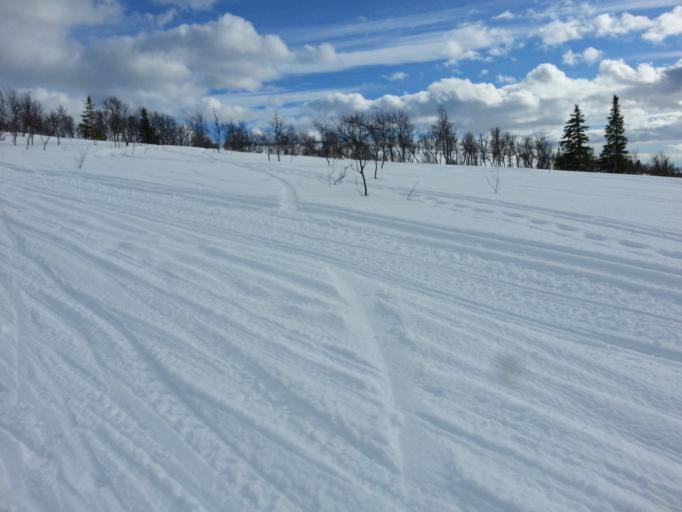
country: NO
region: Nord-Trondelag
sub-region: Royrvik
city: Royrvik
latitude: 64.8520
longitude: 14.1166
